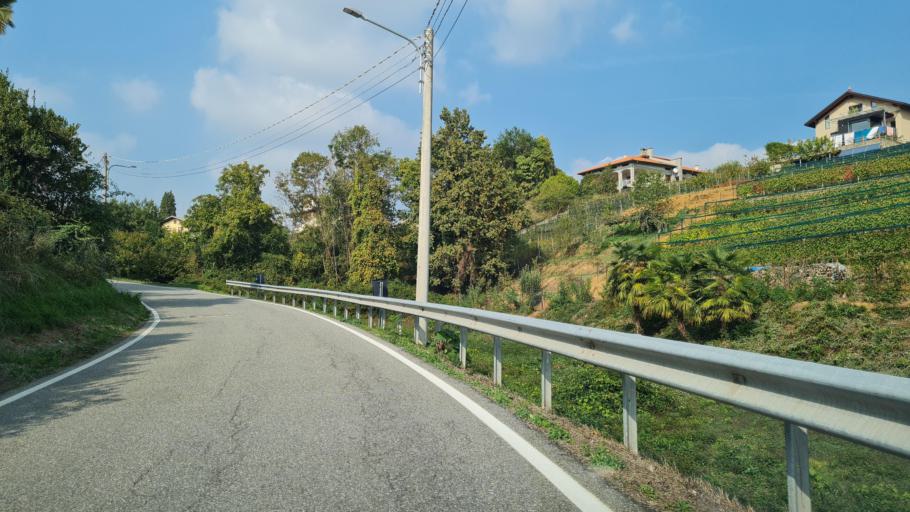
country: IT
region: Piedmont
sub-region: Provincia di Biella
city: Lessona
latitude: 45.5956
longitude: 8.1950
